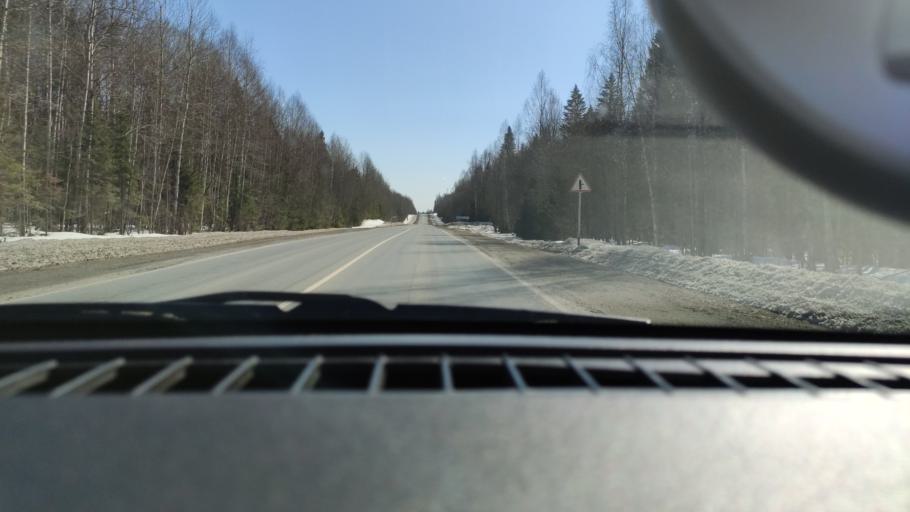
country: RU
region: Perm
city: Perm
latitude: 58.1527
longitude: 56.2546
